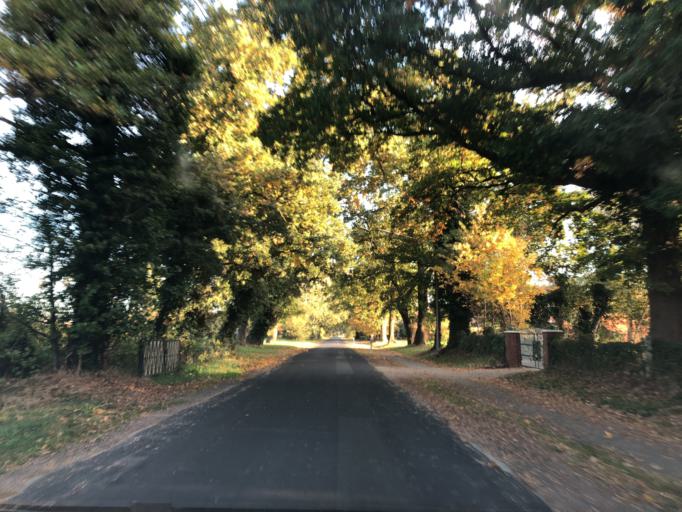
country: DE
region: Lower Saxony
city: Lehe
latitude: 53.0318
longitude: 7.3444
